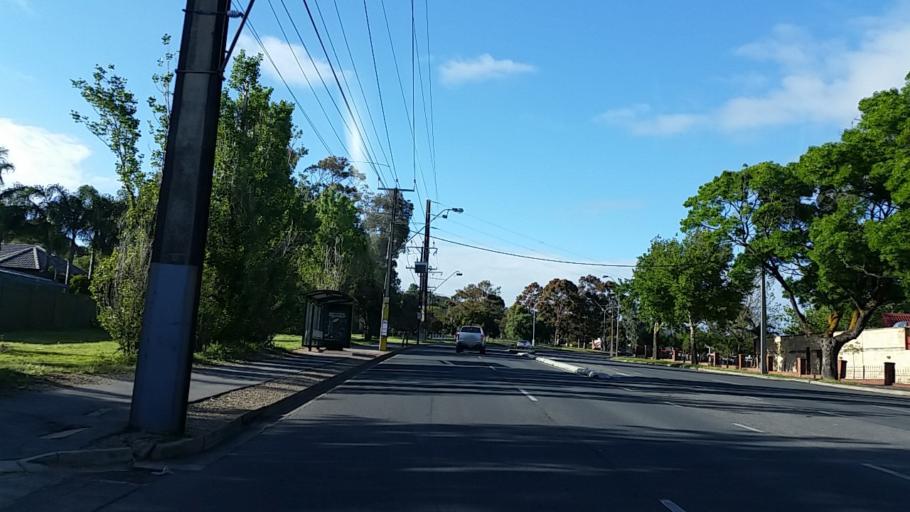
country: AU
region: South Australia
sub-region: Mitcham
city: Clapham
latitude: -34.9981
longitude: 138.5932
